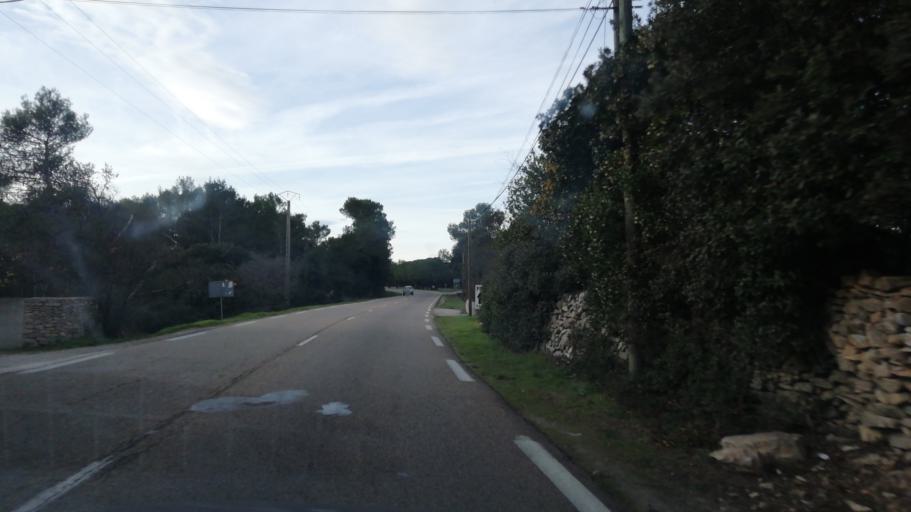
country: FR
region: Languedoc-Roussillon
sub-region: Departement du Gard
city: Caveirac
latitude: 43.8499
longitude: 4.2858
